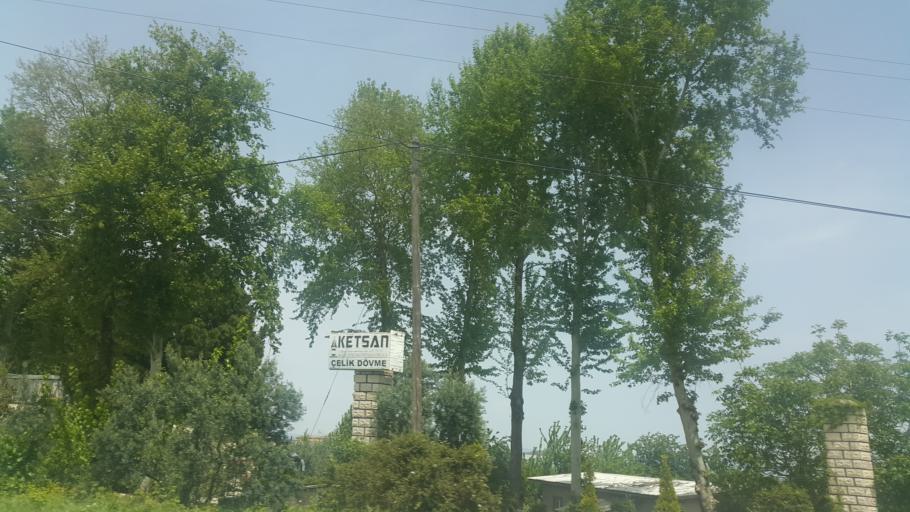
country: TR
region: Osmaniye
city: Toprakkale
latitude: 37.0703
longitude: 36.0930
